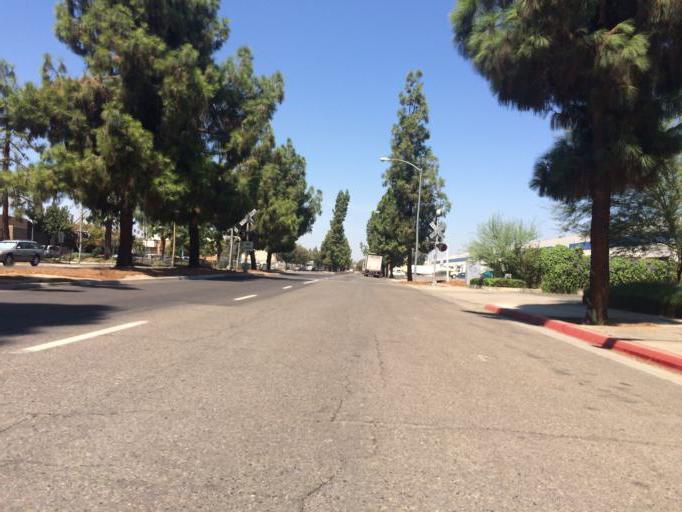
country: US
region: California
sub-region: Fresno County
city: Fresno
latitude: 36.7381
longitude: -119.8014
